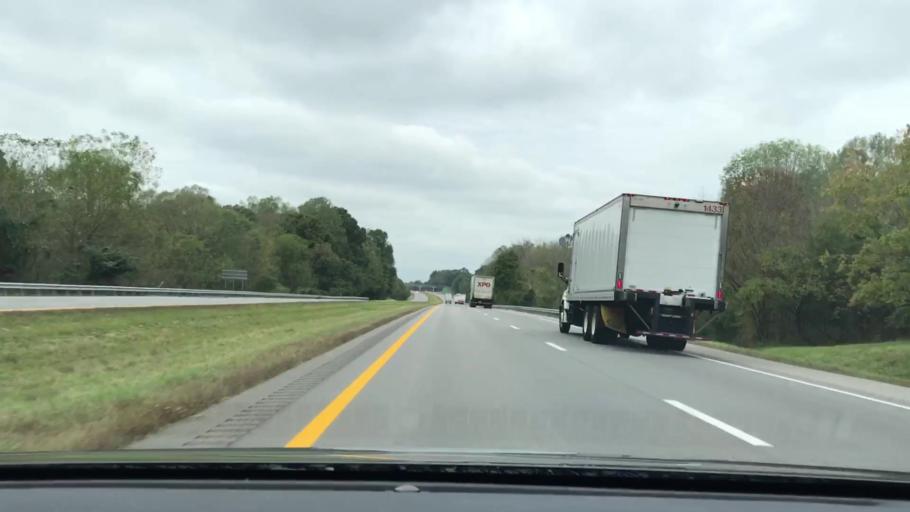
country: US
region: Kentucky
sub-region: Adair County
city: Columbia
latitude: 37.0837
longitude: -85.2543
